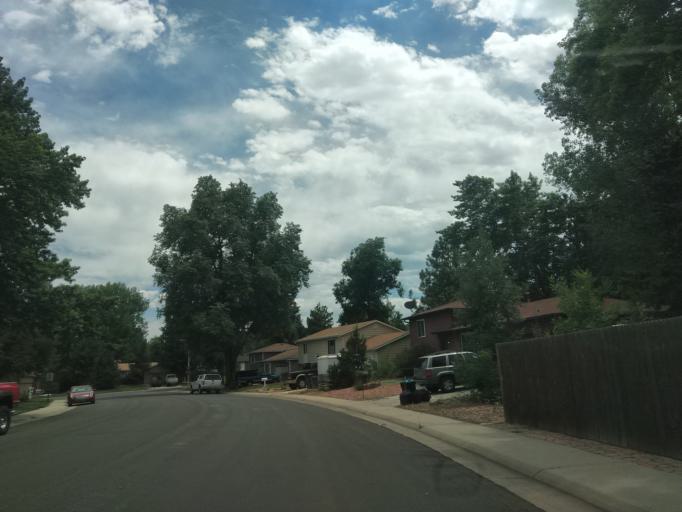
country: US
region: Colorado
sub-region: Jefferson County
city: Lakewood
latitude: 39.6881
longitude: -105.1230
